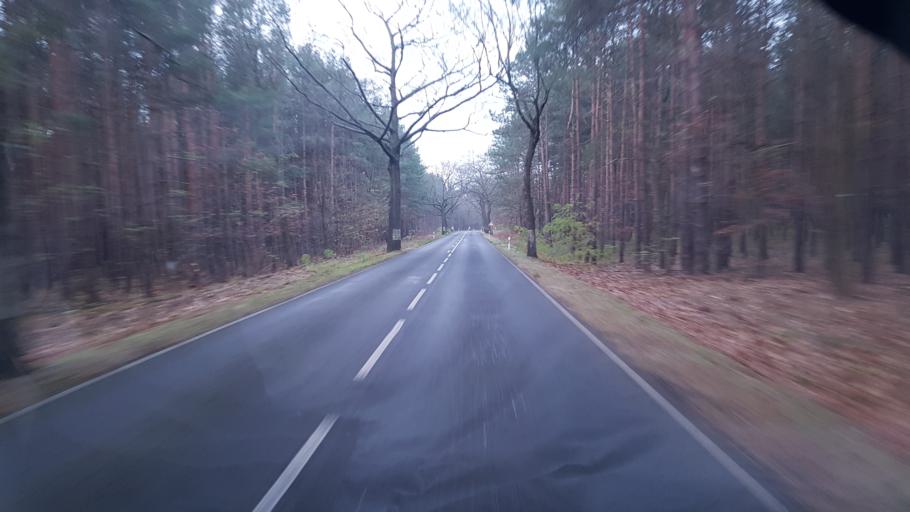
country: DE
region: Brandenburg
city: Gross Lindow
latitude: 52.1842
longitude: 14.5189
